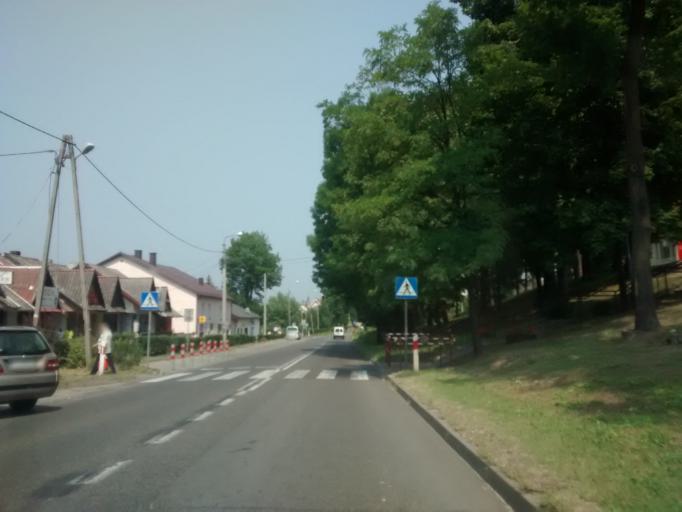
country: PL
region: Lesser Poland Voivodeship
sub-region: Powiat olkuski
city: Klucze
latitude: 50.3374
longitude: 19.5621
